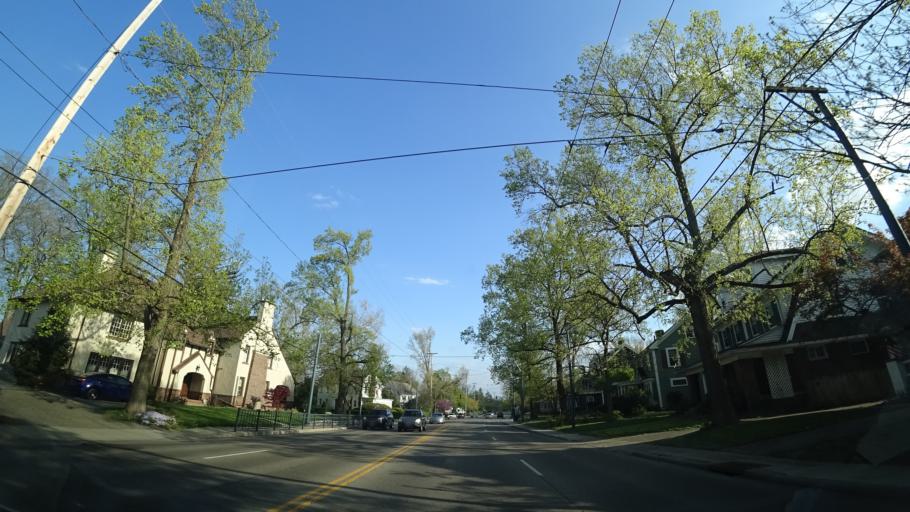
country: US
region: Ohio
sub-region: Montgomery County
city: Oakwood
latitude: 39.7242
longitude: -84.1734
